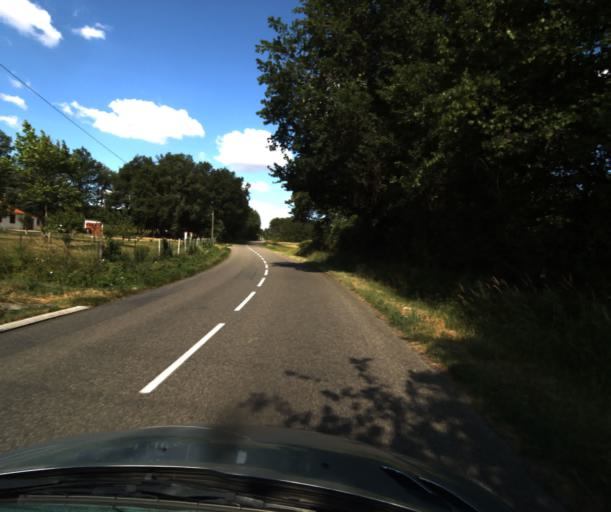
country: FR
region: Midi-Pyrenees
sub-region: Departement du Tarn-et-Garonne
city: Campsas
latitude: 43.9021
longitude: 1.3019
